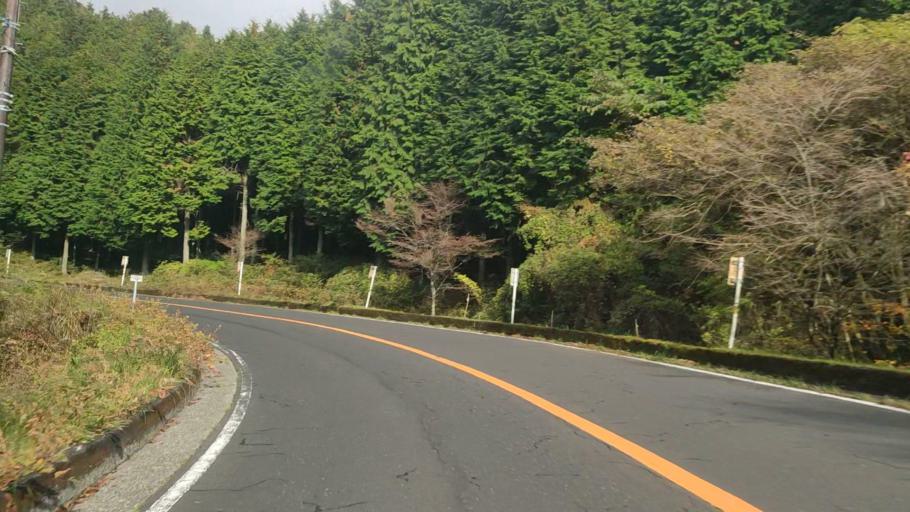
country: JP
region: Shizuoka
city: Fujinomiya
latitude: 35.3037
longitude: 138.6780
